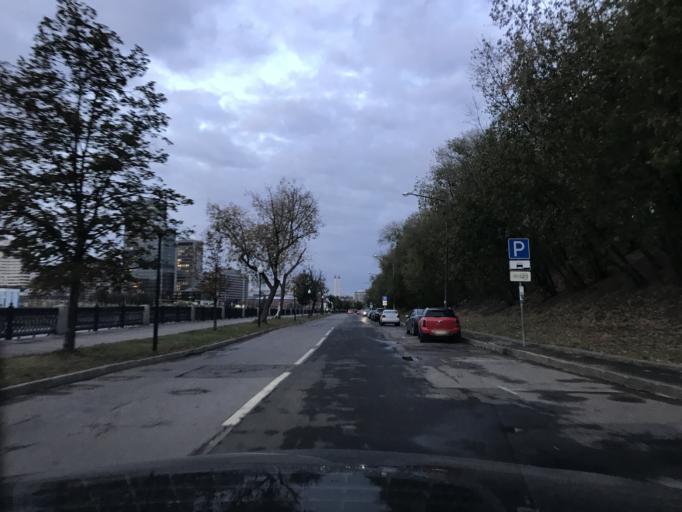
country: RU
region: Moskovskaya
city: Presnenskiy
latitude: 55.7489
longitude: 37.5511
